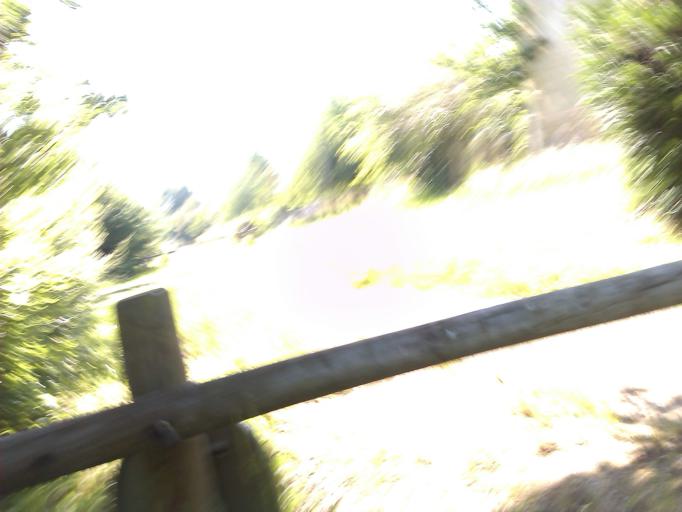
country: FR
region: Centre
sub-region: Departement de l'Indre
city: Belabre
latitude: 46.6310
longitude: 1.2549
